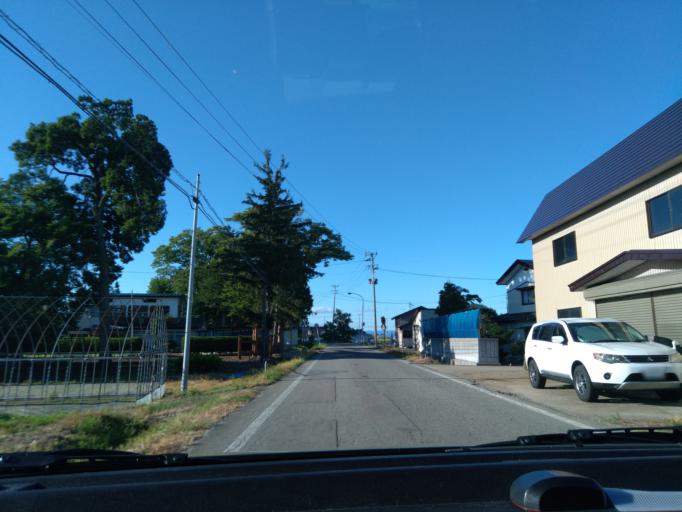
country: JP
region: Akita
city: Omagari
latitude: 39.4194
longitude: 140.5145
